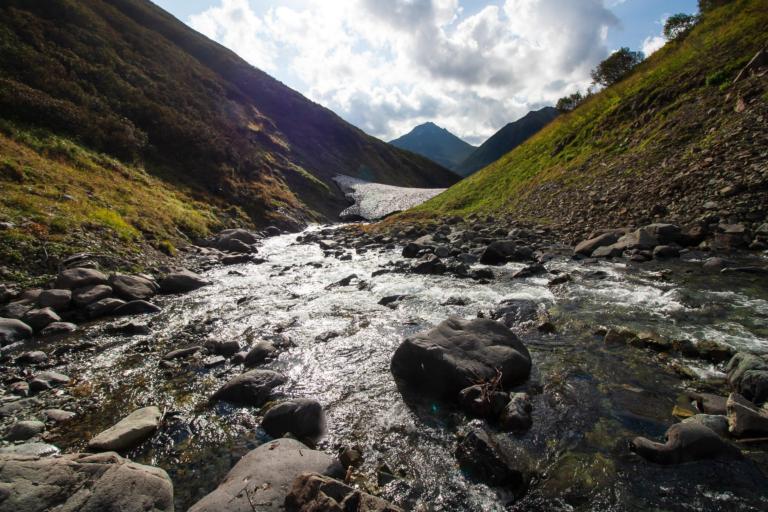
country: RU
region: Kamtsjatka
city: Yelizovo
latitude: 53.8411
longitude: 158.2735
